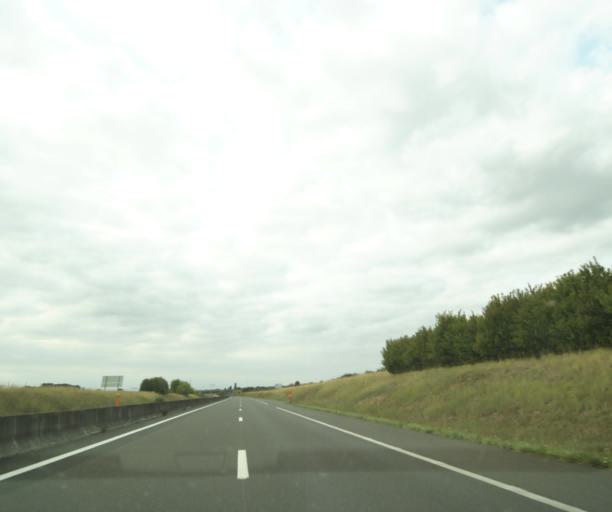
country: FR
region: Centre
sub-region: Departement d'Indre-et-Loire
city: Parcay-Meslay
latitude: 47.4707
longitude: 0.7597
